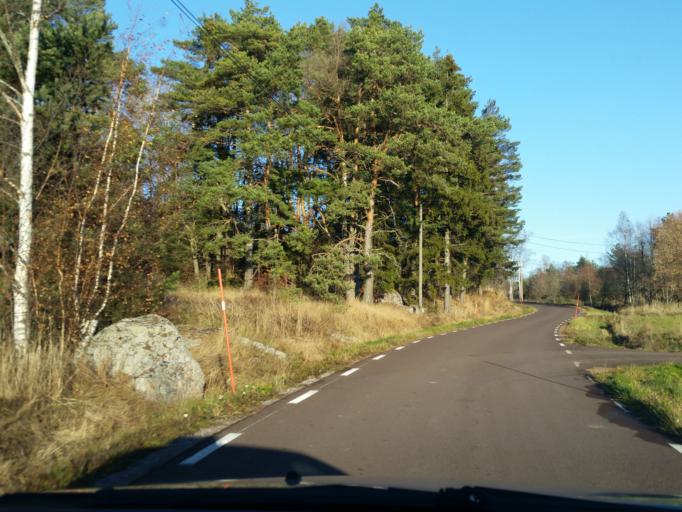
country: AX
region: Alands skaergard
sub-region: Braendoe
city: Braendoe
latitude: 60.4142
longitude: 21.0514
